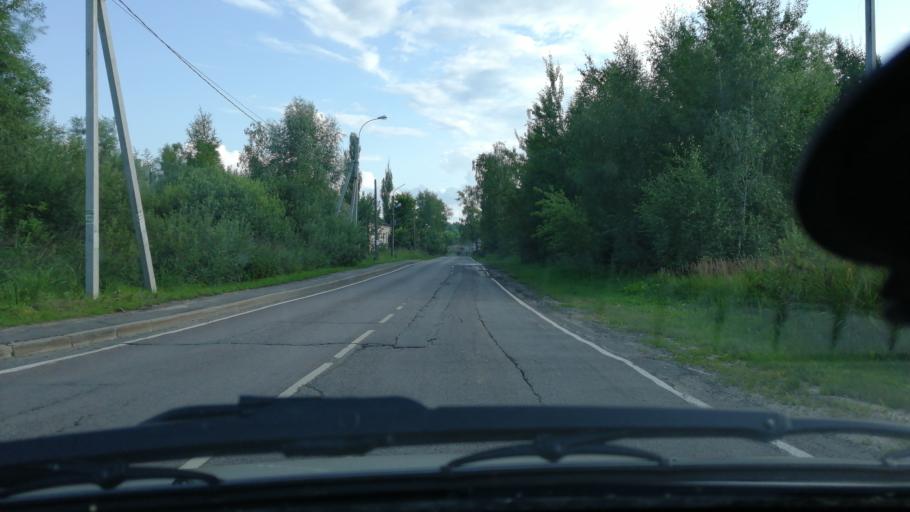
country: RU
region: Moskovskaya
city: Troitskoye
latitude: 55.2834
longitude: 38.5415
